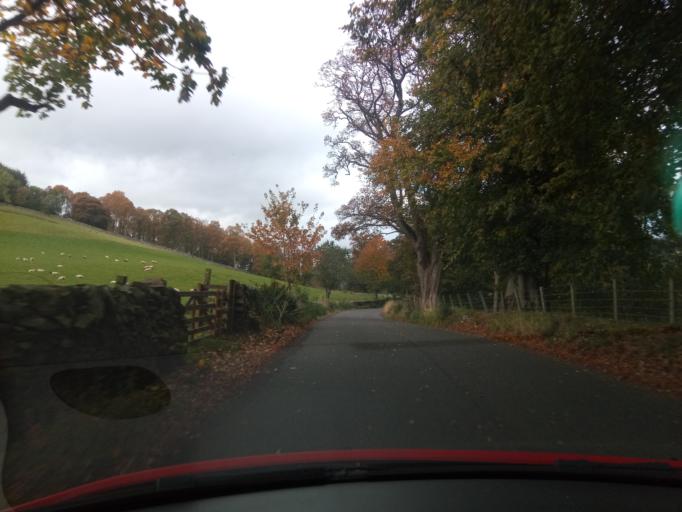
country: GB
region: Scotland
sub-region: The Scottish Borders
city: Peebles
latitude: 55.6394
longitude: -3.1492
